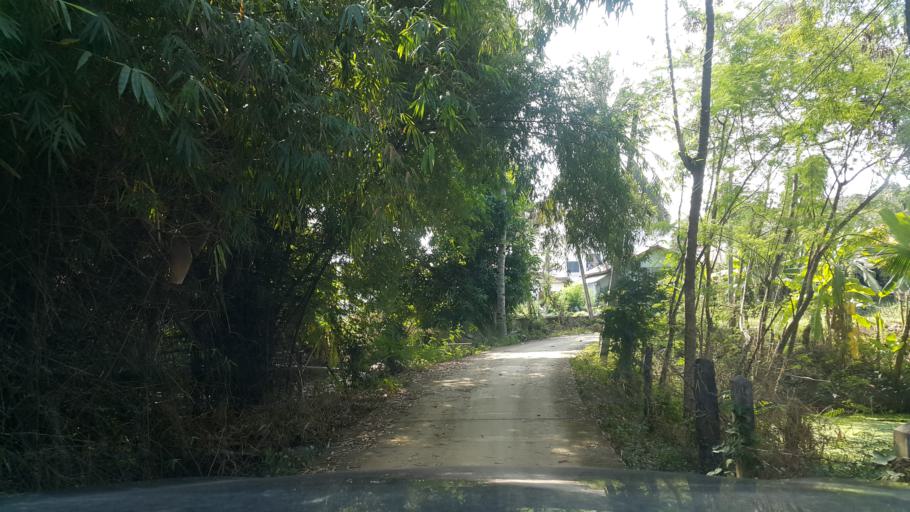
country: TH
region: Sukhothai
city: Thung Saliam
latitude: 17.3191
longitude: 99.5531
